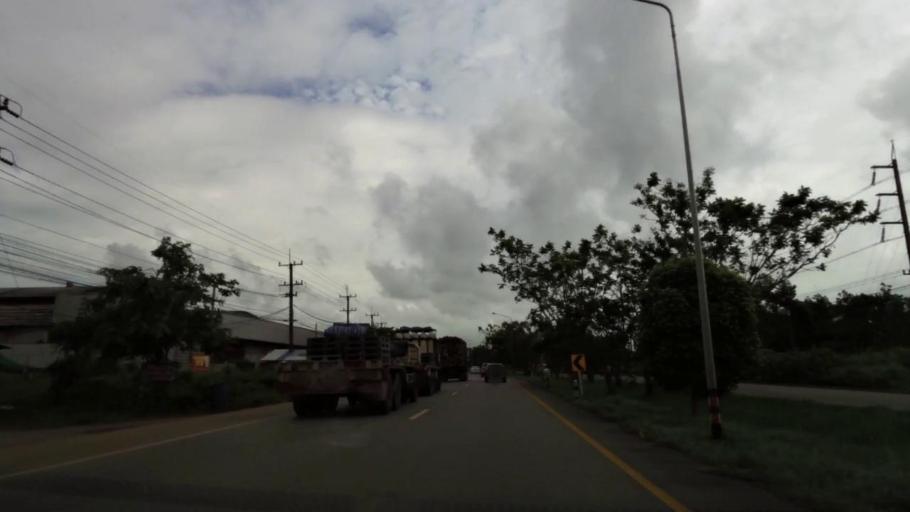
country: TH
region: Chanthaburi
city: Na Yai Am
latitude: 12.7305
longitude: 101.9162
